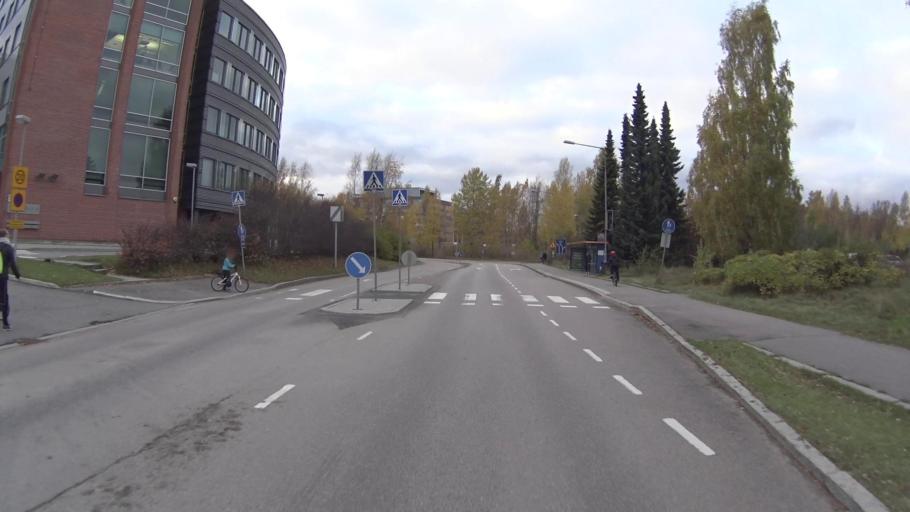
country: FI
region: Uusimaa
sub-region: Helsinki
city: Otaniemi
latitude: 60.1857
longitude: 24.8135
